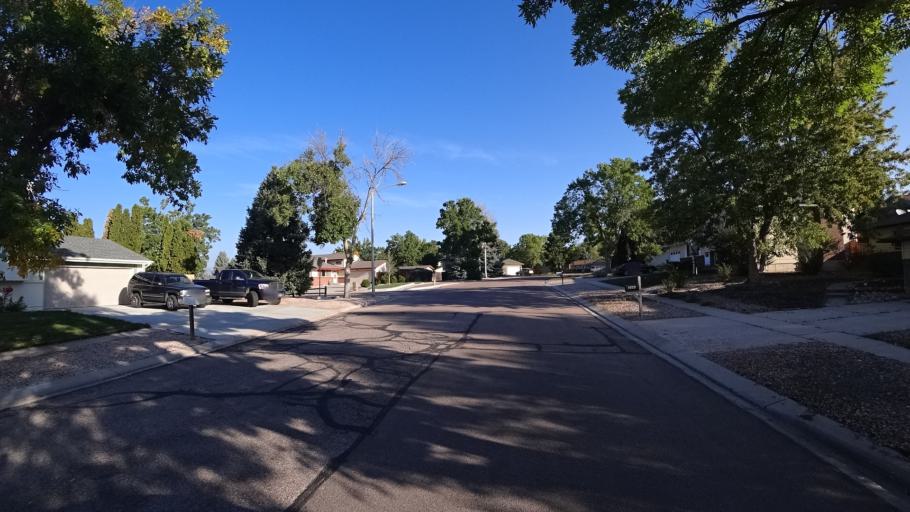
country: US
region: Colorado
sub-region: El Paso County
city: Cimarron Hills
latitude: 38.8810
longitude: -104.7467
